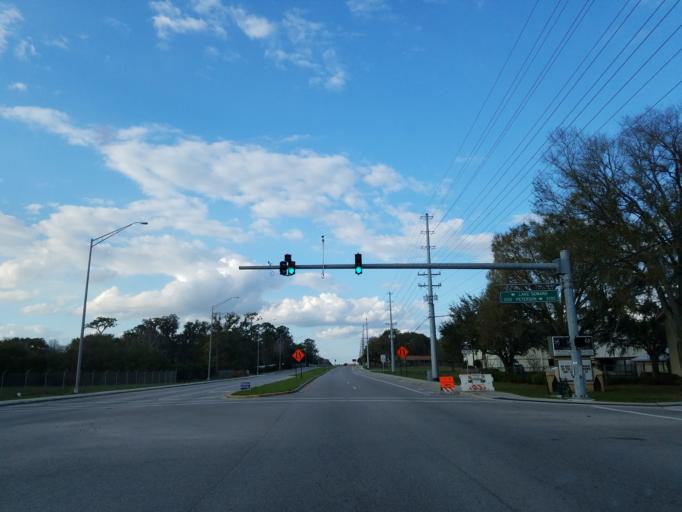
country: US
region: Florida
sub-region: Polk County
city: Lakeland Highlands
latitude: 27.9600
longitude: -81.9236
